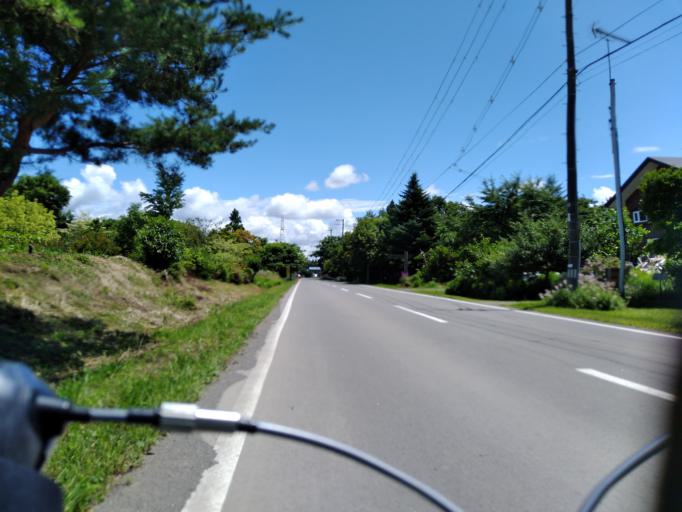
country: JP
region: Iwate
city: Shizukuishi
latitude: 39.7583
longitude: 140.9825
